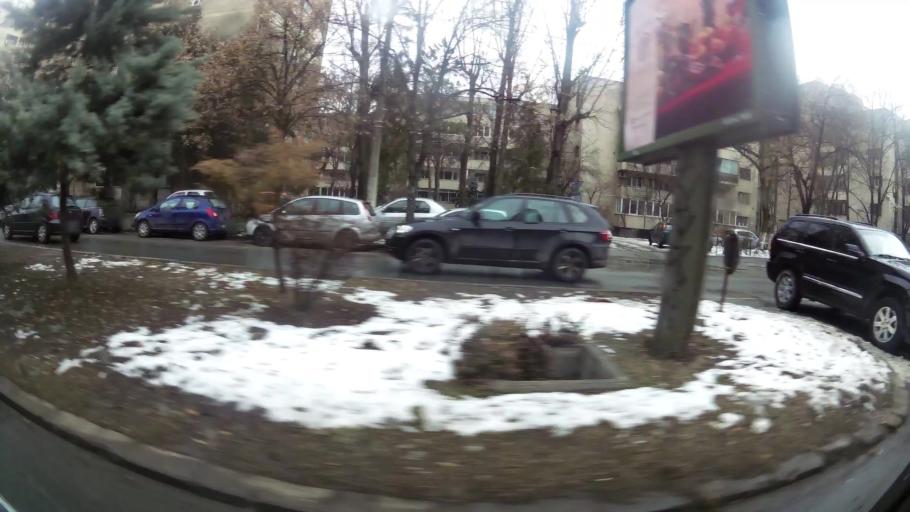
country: RO
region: Ilfov
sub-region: Comuna Chiajna
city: Rosu
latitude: 44.4217
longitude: 26.0476
